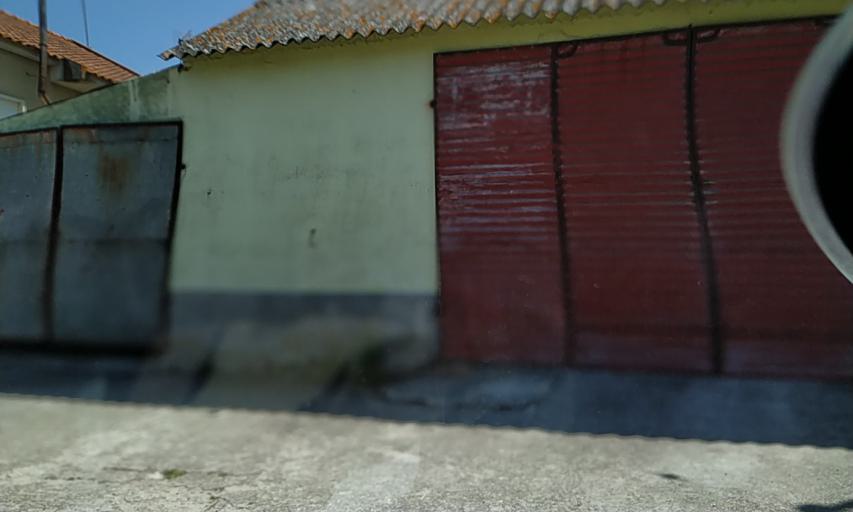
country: PT
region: Setubal
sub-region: Palmela
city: Palmela
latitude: 38.6059
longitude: -8.7808
